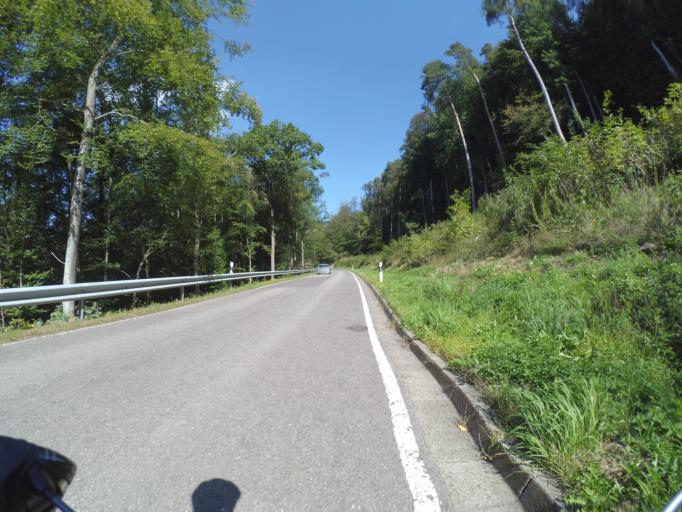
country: DE
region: Rheinland-Pfalz
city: Budlich
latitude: 49.7781
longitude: 6.8979
